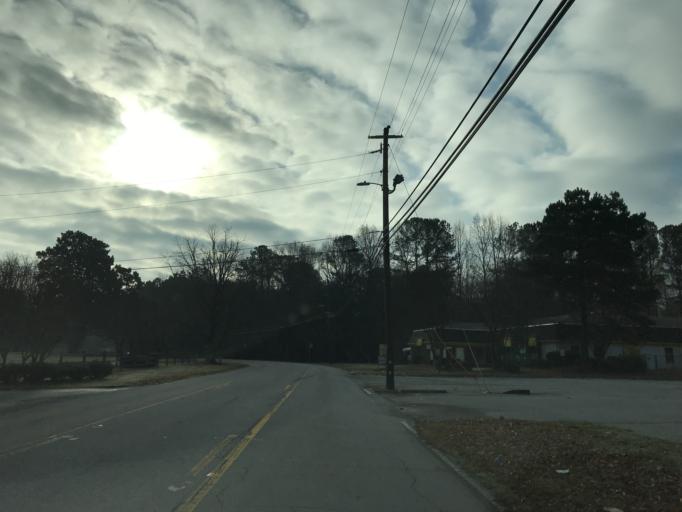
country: US
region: Georgia
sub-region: Clayton County
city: Riverdale
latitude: 33.5764
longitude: -84.3819
